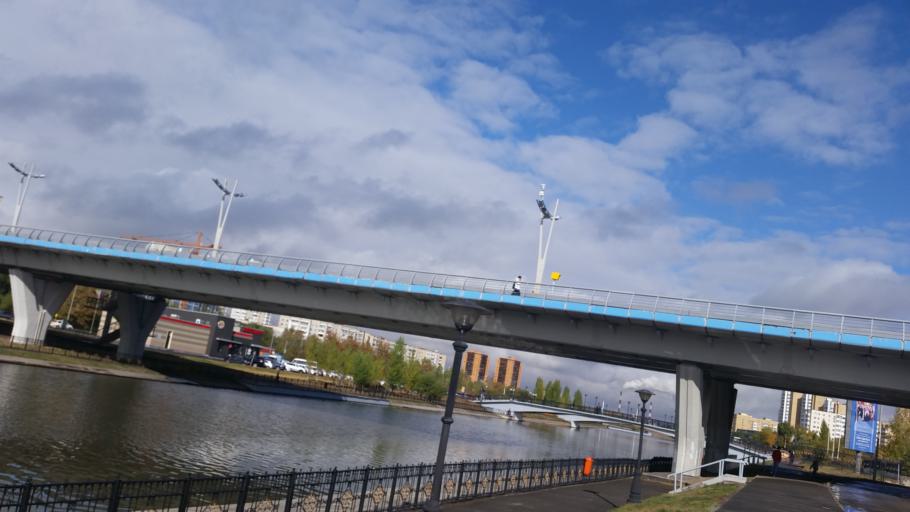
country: KZ
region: Astana Qalasy
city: Astana
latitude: 51.1578
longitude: 71.4652
